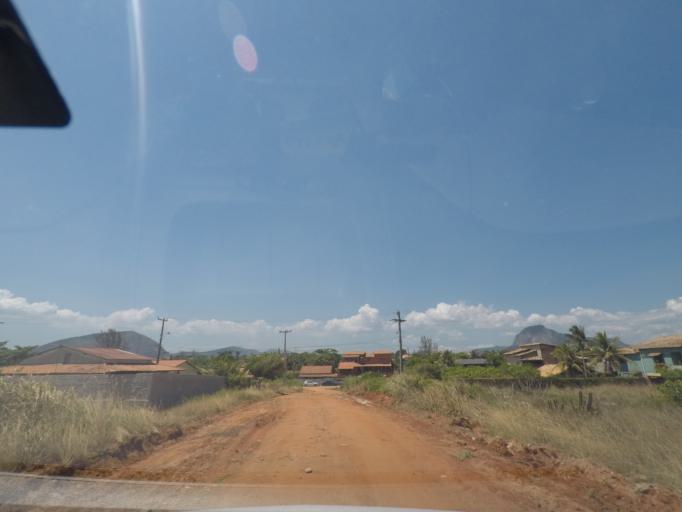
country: BR
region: Rio de Janeiro
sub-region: Marica
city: Marica
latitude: -22.9715
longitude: -42.9414
